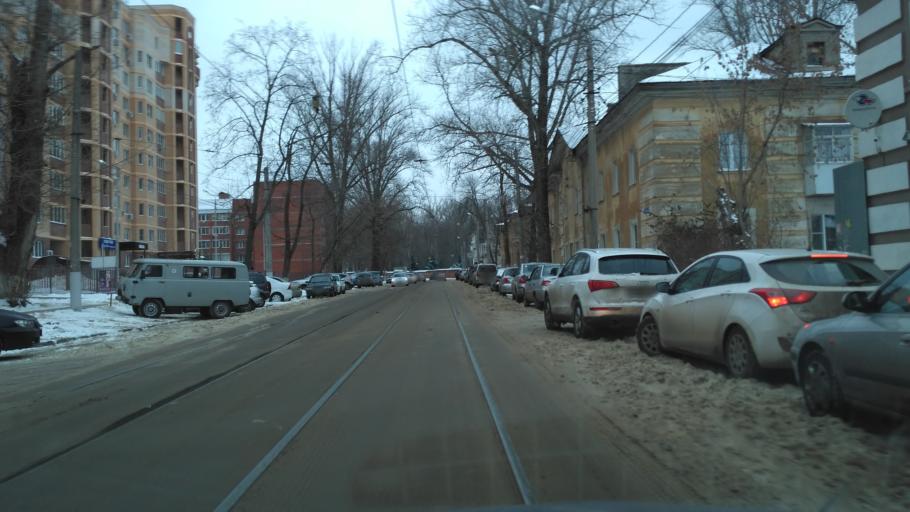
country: RU
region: Tula
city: Tula
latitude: 54.1751
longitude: 37.6154
